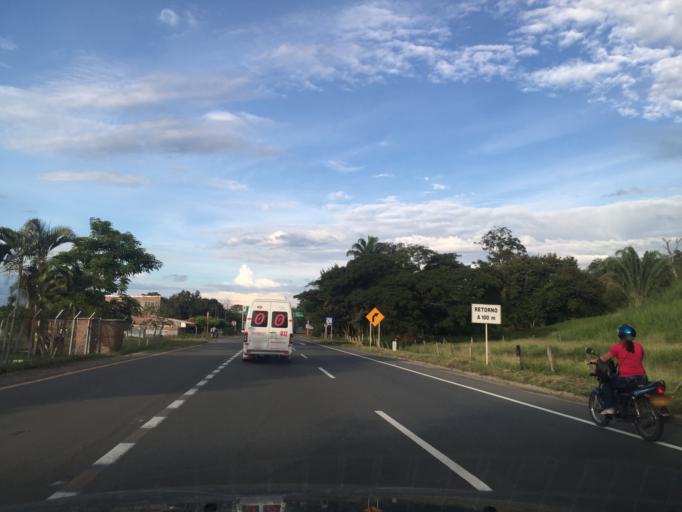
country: CO
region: Valle del Cauca
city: Bugalagrande
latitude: 4.2354
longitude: -76.1310
